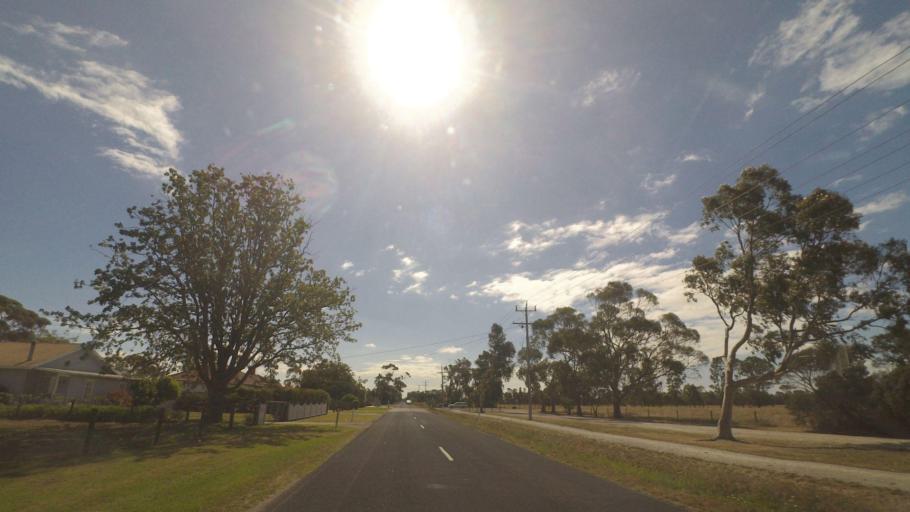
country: AU
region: Victoria
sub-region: Cardinia
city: Pakenham South
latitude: -38.1765
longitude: 145.5675
